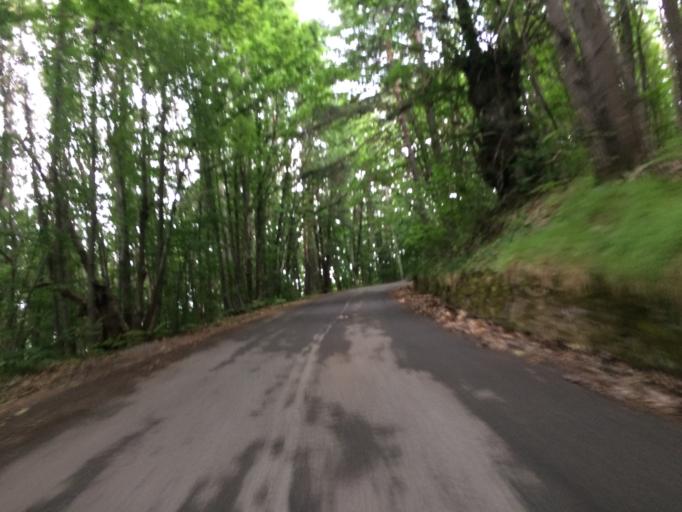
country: IT
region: Liguria
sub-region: Provincia di Imperia
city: Triora
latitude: 43.9831
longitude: 7.7509
